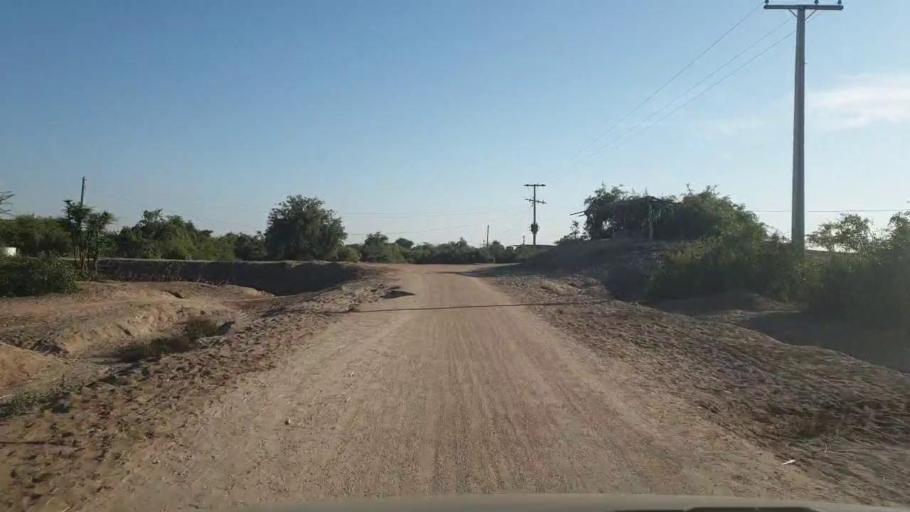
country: PK
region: Sindh
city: Dhoro Naro
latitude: 25.4250
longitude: 69.5438
